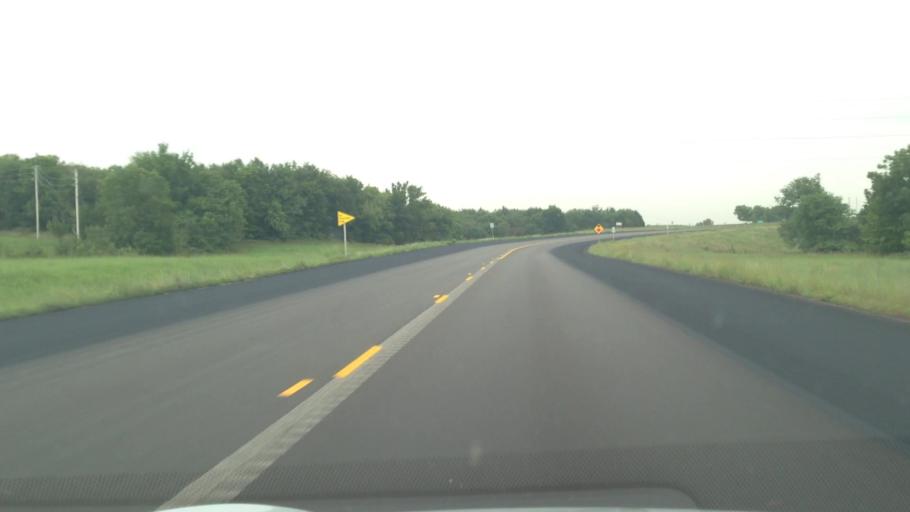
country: US
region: Kansas
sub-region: Cherokee County
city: Baxter Springs
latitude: 37.0282
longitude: -94.7030
